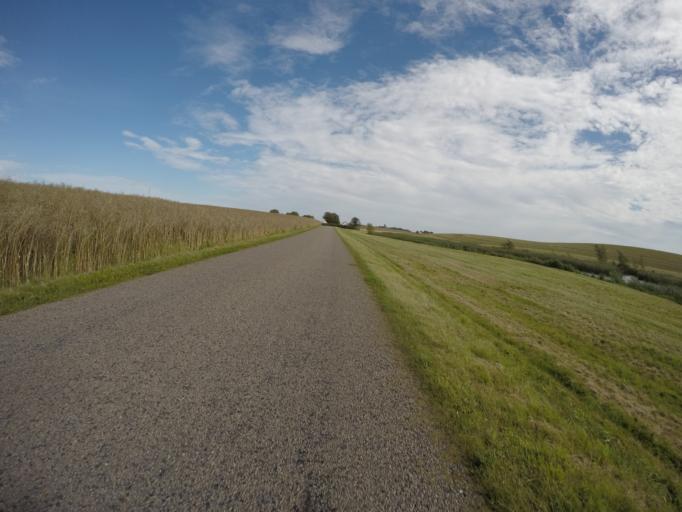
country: SE
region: Skane
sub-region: Simrishamns Kommun
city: Simrishamn
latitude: 55.4978
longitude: 14.2321
